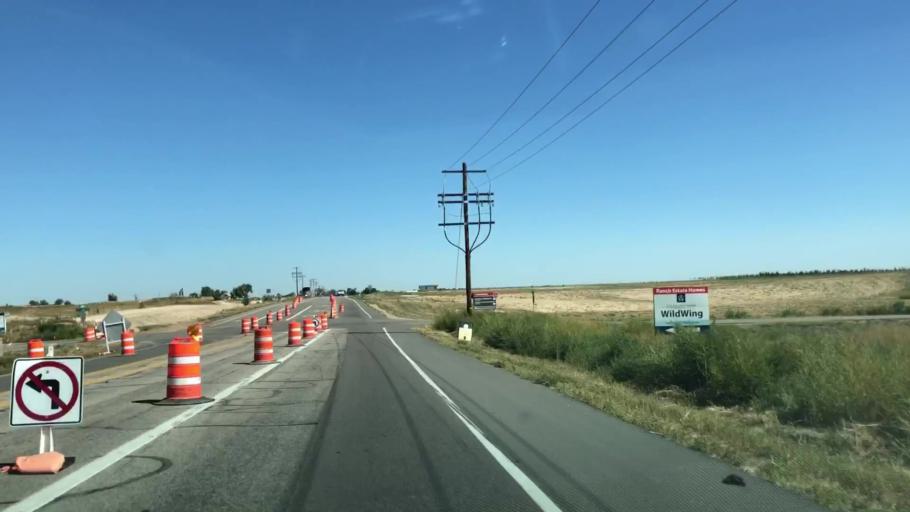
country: US
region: Colorado
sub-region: Weld County
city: Windsor
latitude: 40.5227
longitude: -104.9451
